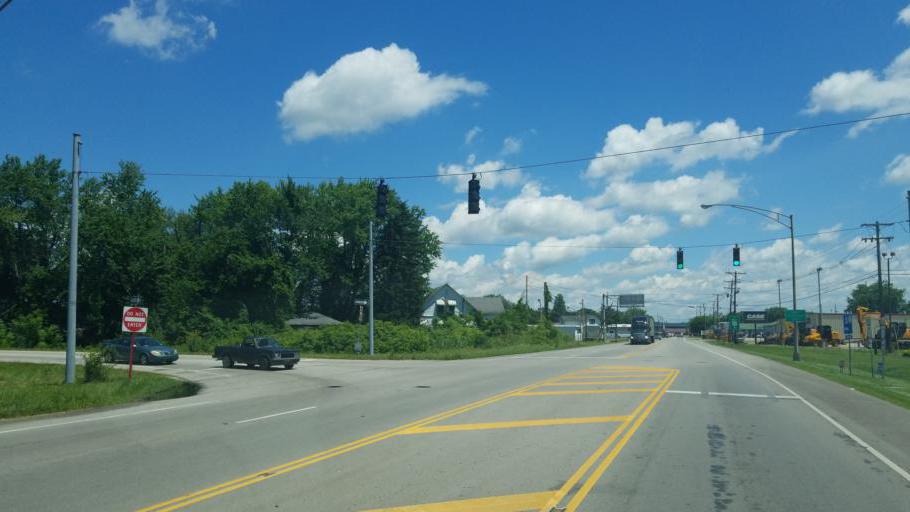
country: US
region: West Virginia
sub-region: Mason County
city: Point Pleasant
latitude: 38.8386
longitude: -82.1504
